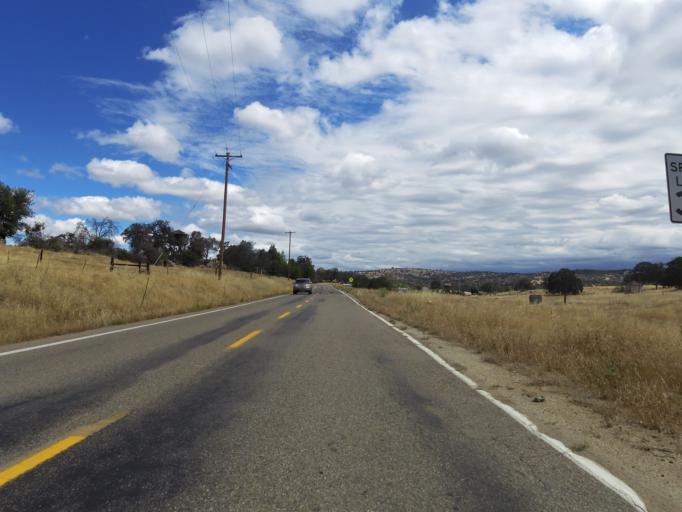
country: US
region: California
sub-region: Madera County
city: Yosemite Lakes
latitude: 37.2078
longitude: -119.9080
